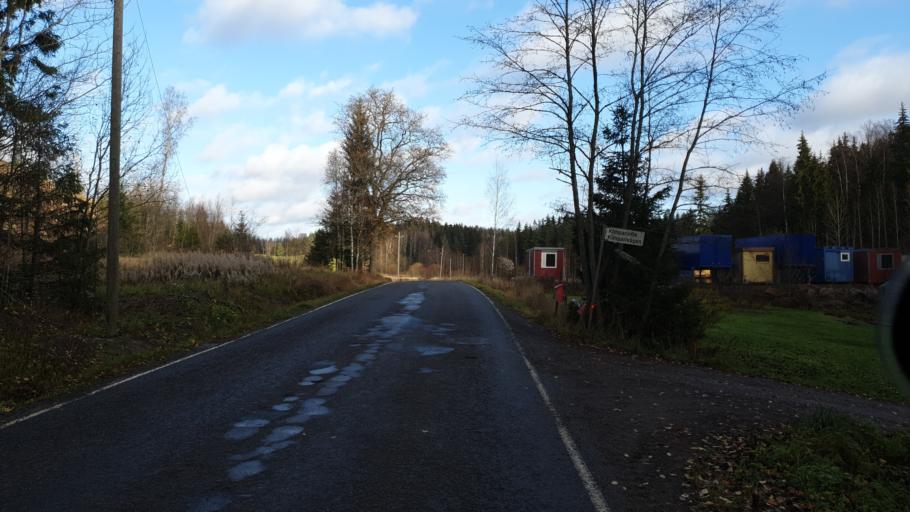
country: FI
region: Uusimaa
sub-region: Helsinki
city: Siuntio
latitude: 60.2653
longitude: 24.3041
